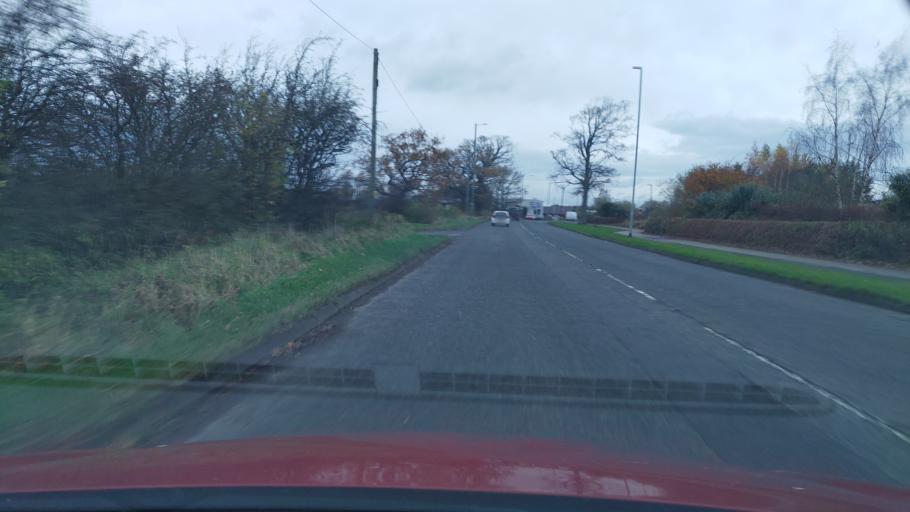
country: GB
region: England
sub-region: Lancashire
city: Euxton
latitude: 53.6847
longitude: -2.6765
